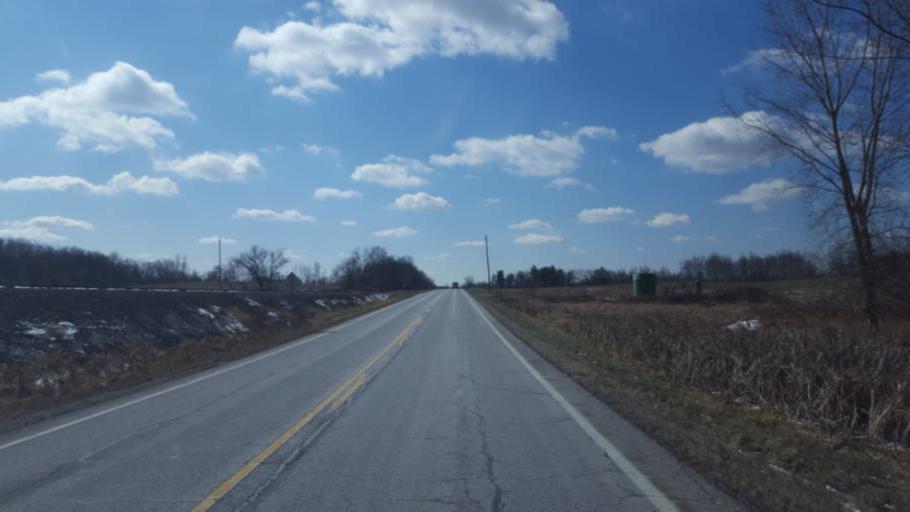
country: US
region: Ohio
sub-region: Licking County
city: Utica
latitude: 40.2598
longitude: -82.4512
